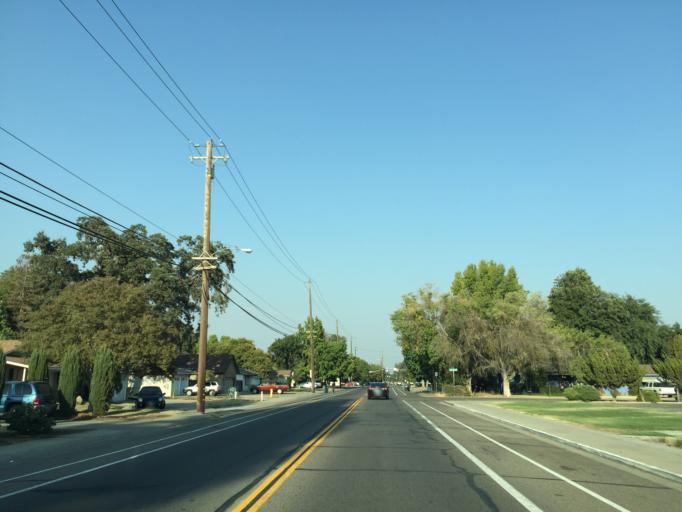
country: US
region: California
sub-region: Tulare County
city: Visalia
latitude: 36.3201
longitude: -119.3084
